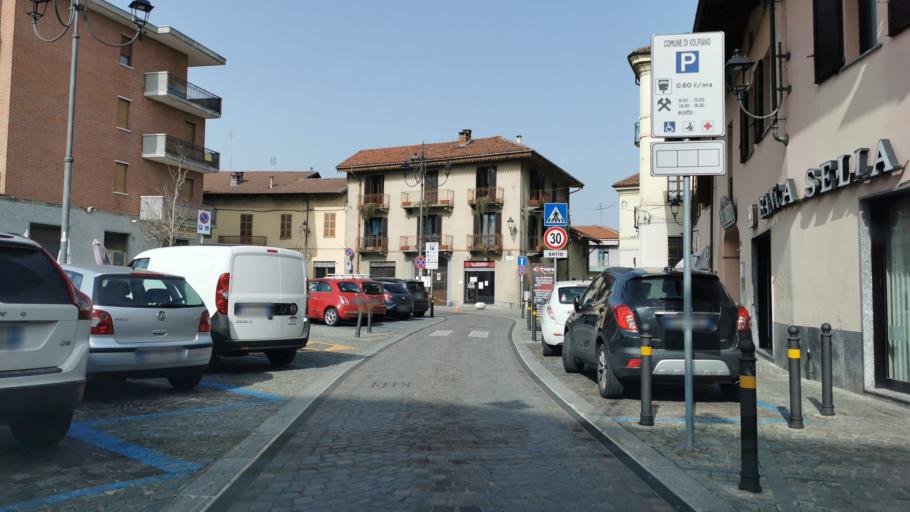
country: IT
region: Piedmont
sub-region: Provincia di Torino
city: Volpiano
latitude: 45.2015
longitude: 7.7773
